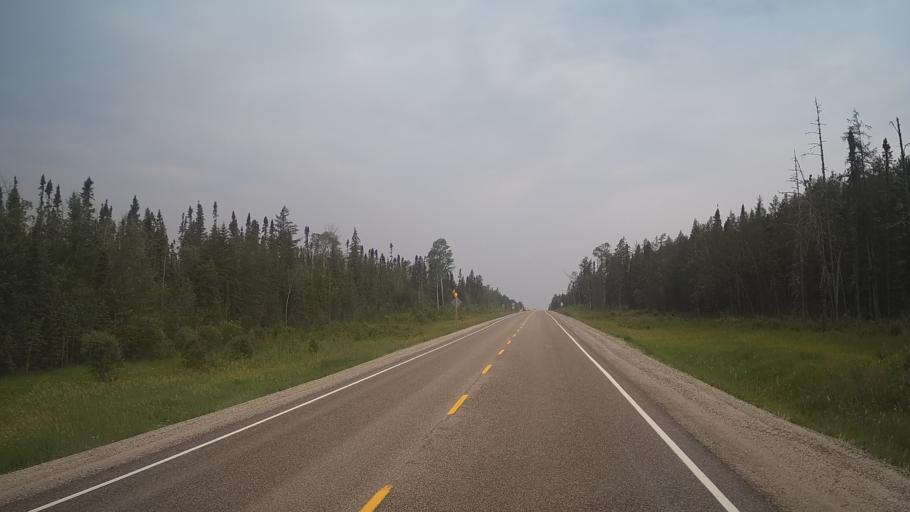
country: CA
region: Ontario
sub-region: Algoma
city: Hornepayne
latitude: 49.7556
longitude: -85.0005
